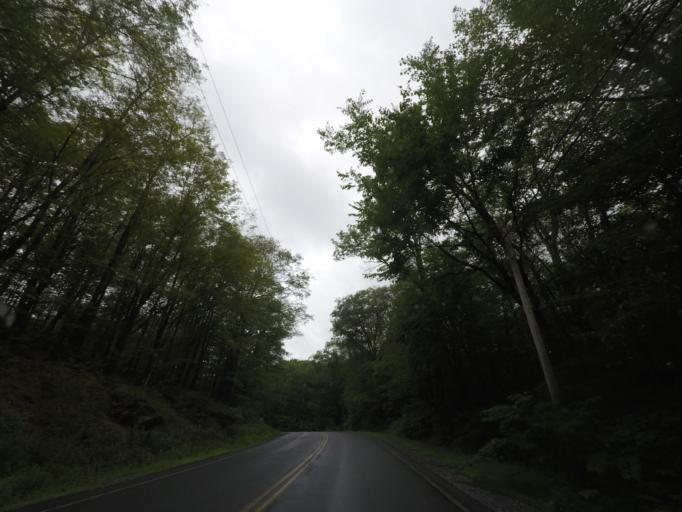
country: US
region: New York
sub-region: Rensselaer County
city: Poestenkill
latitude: 42.6970
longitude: -73.3910
